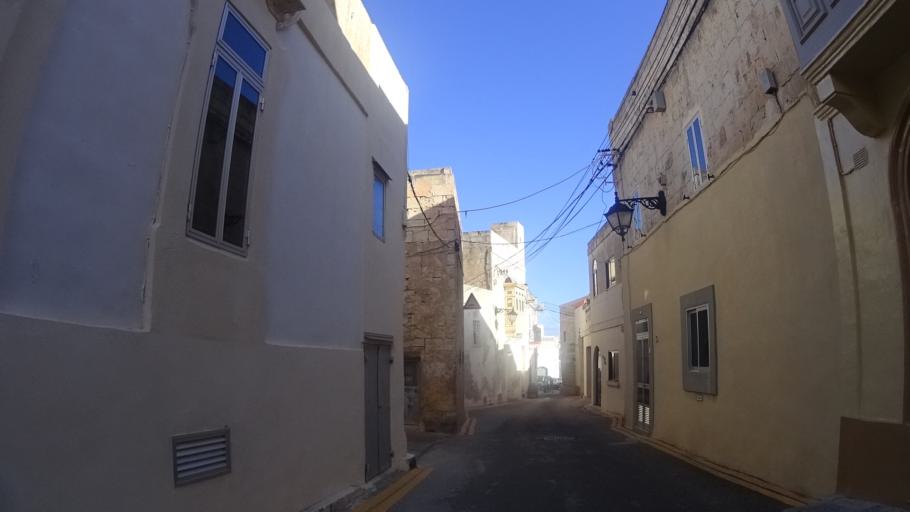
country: MT
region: Hal Gharghur
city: Hal Gharghur
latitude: 35.9250
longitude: 14.4528
